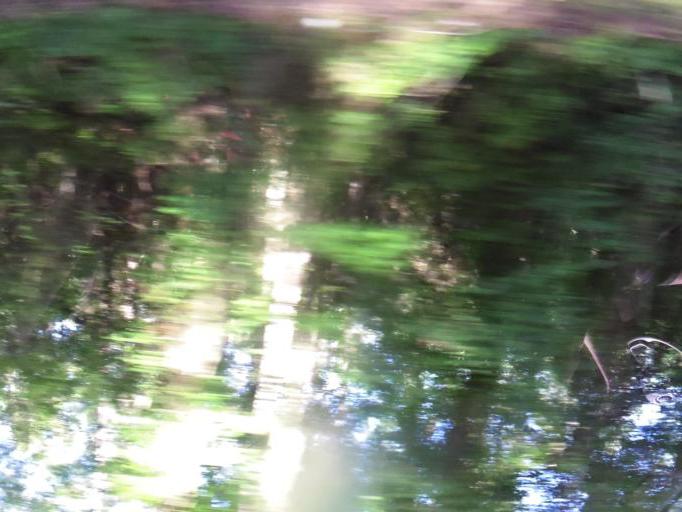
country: US
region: Florida
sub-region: Nassau County
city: Nassau Village-Ratliff
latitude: 30.4754
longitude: -81.7846
